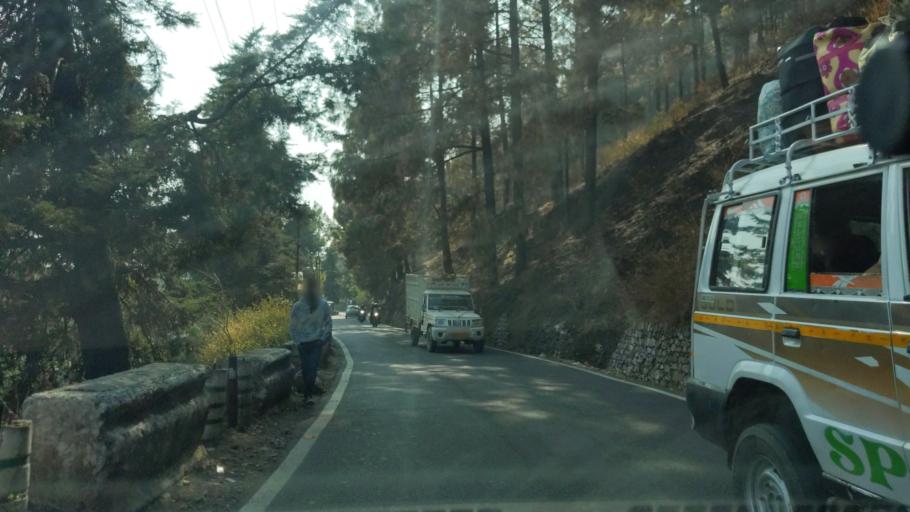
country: IN
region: Uttarakhand
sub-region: Naini Tal
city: Bhowali
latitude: 29.3804
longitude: 79.5186
